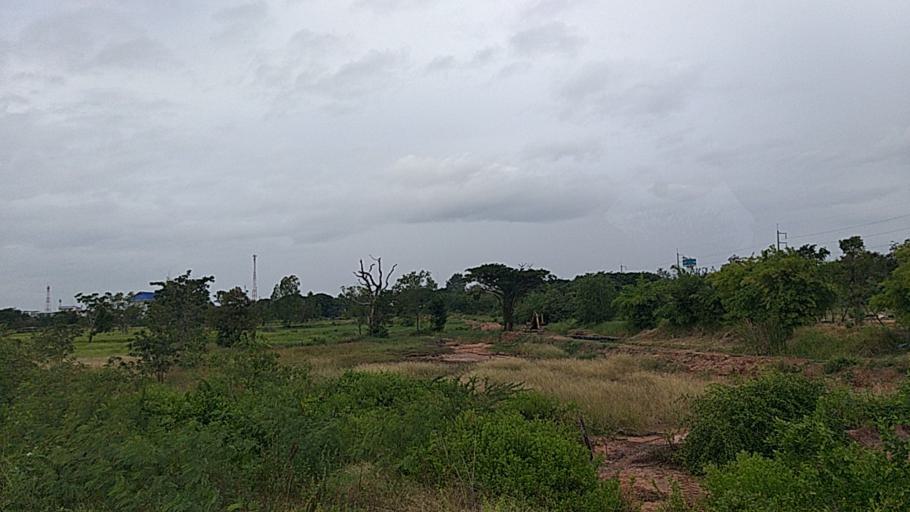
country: TH
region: Maha Sarakham
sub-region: Amphoe Borabue
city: Borabue
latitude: 16.0403
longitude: 103.1283
